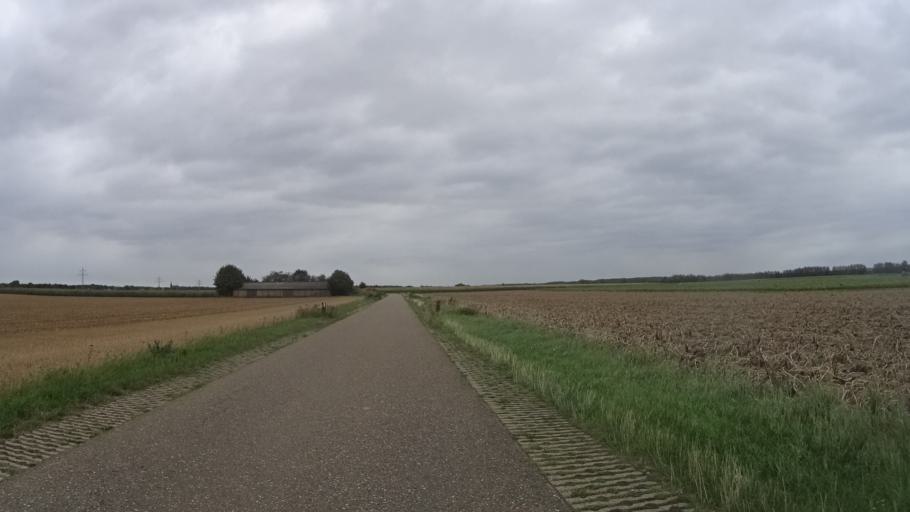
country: NL
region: Limburg
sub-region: Gemeente Leudal
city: Haelen
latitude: 51.2379
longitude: 5.9807
